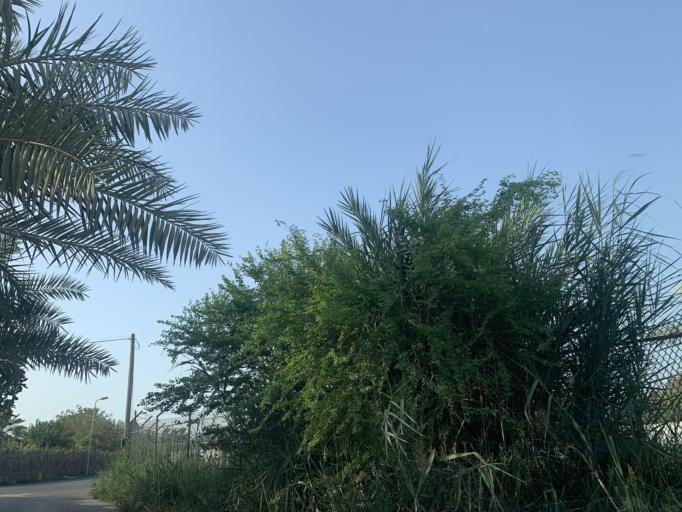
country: BH
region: Central Governorate
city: Madinat Hamad
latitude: 26.1877
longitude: 50.4619
